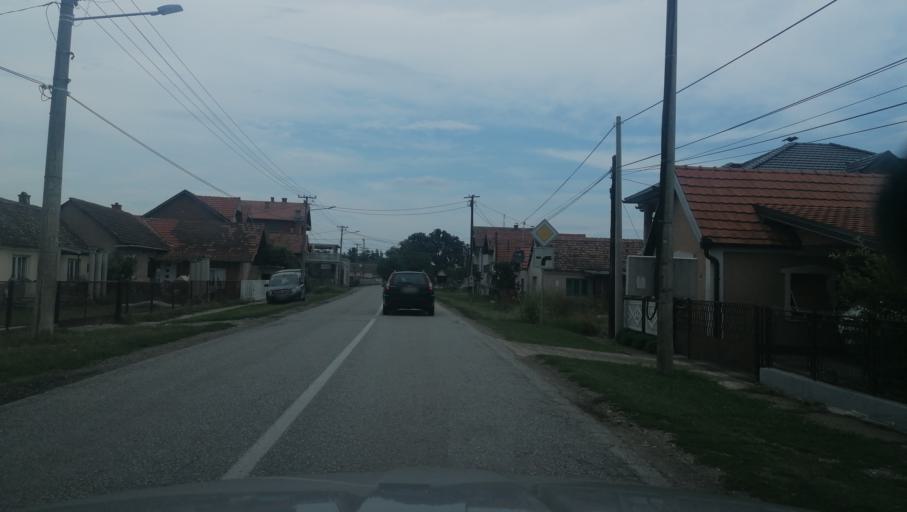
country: RS
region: Central Serbia
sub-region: Macvanski Okrug
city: Bogatic
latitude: 44.8335
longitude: 19.4702
